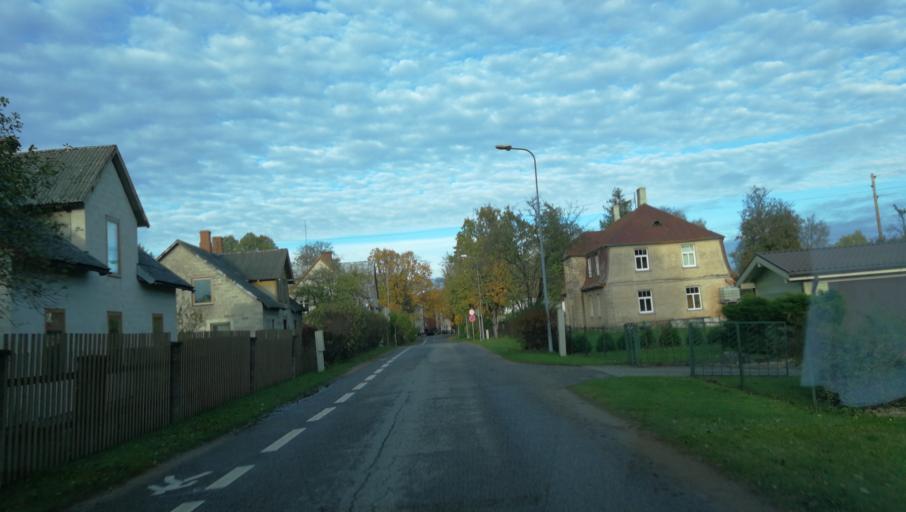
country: LV
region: Cesu Rajons
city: Cesis
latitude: 57.3037
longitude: 25.2656
